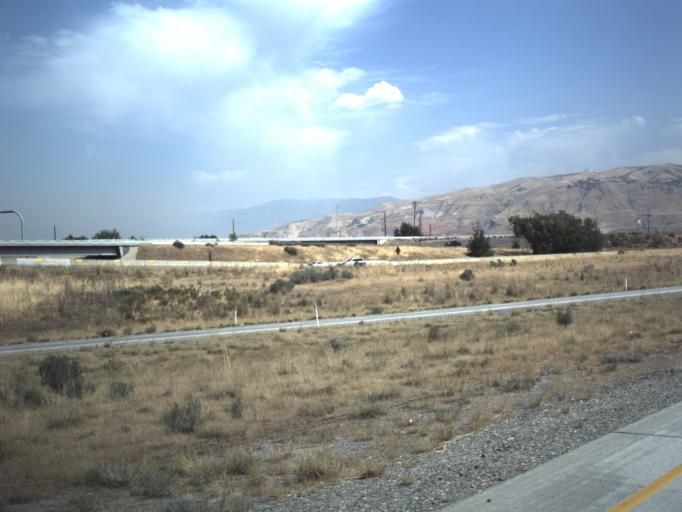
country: US
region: Utah
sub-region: Salt Lake County
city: Salt Lake City
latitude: 40.7644
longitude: -111.9471
